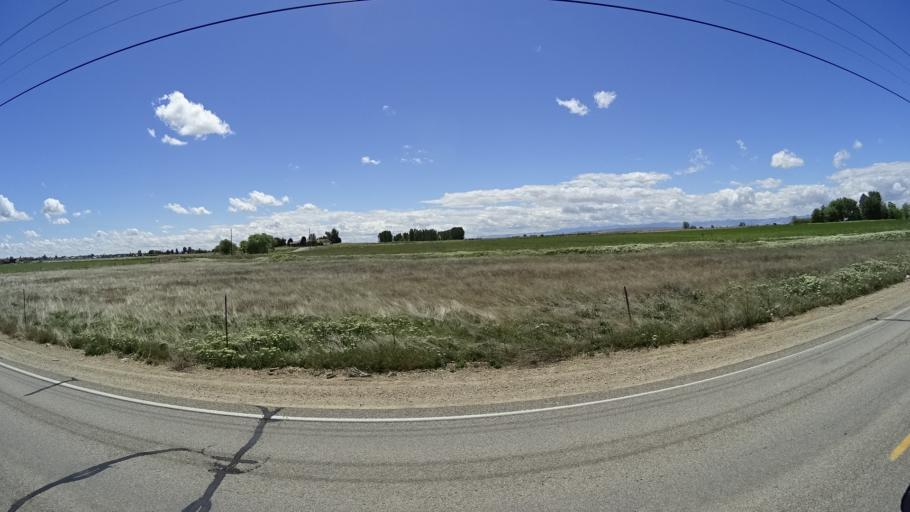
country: US
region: Idaho
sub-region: Ada County
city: Meridian
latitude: 43.5466
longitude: -116.3801
